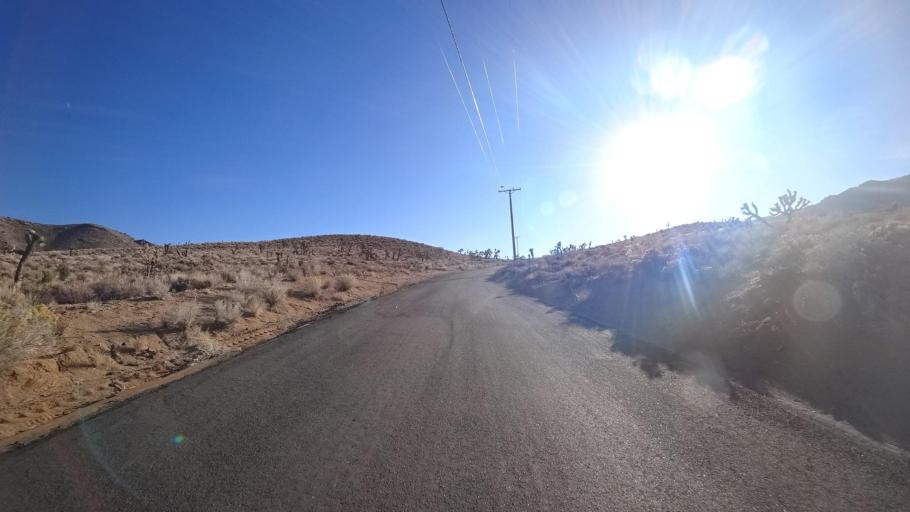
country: US
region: California
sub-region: Kern County
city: Weldon
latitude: 35.5224
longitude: -118.2003
